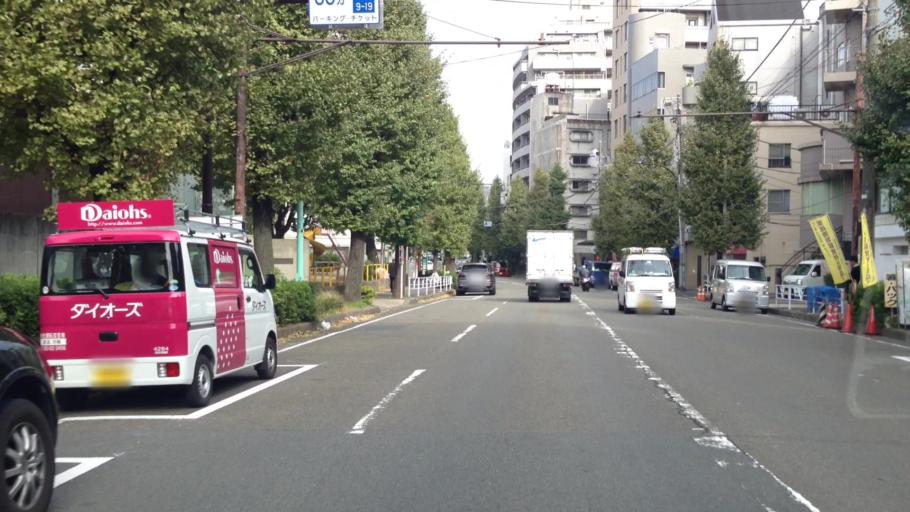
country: JP
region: Tokyo
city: Tokyo
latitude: 35.6536
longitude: 139.7136
